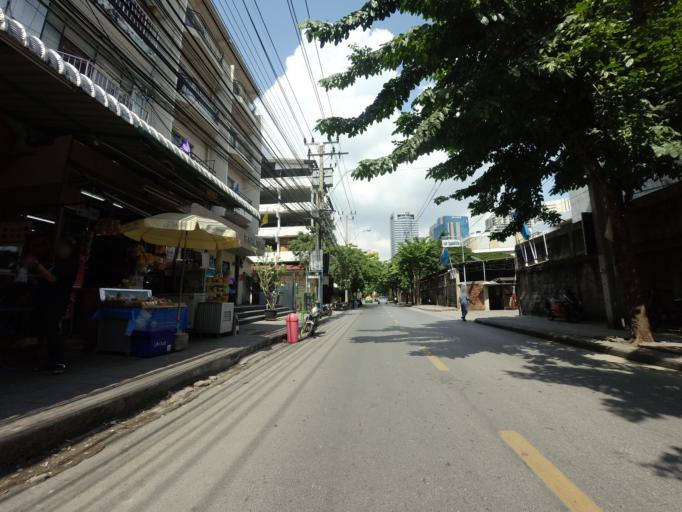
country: TH
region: Bangkok
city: Bang Sue
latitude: 13.8039
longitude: 100.5565
